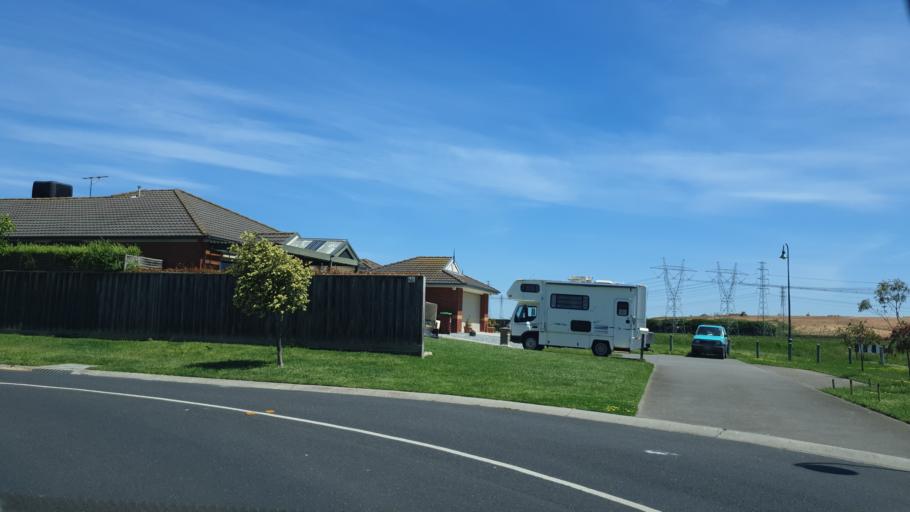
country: AU
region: Victoria
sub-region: Casey
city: Narre Warren South
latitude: -38.0597
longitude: 145.2819
